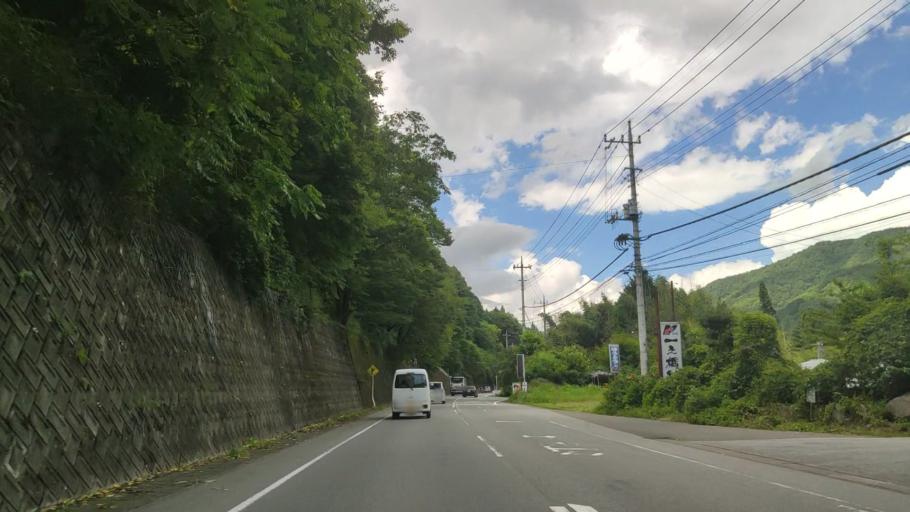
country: JP
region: Yamanashi
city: Enzan
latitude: 35.7675
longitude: 138.7364
